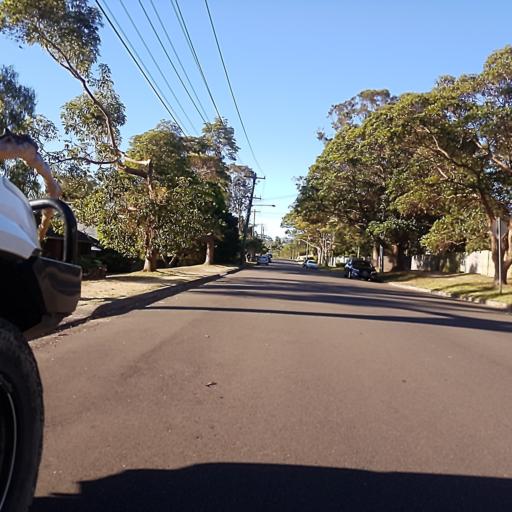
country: AU
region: New South Wales
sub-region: Warringah
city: Forestville
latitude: -33.7564
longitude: 151.2147
